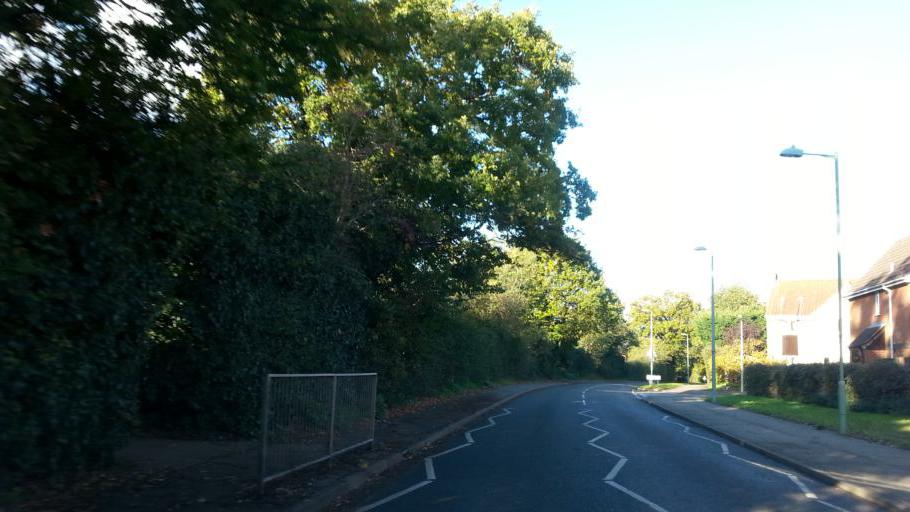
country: GB
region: England
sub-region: Suffolk
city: Thurston
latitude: 52.2520
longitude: 0.8106
